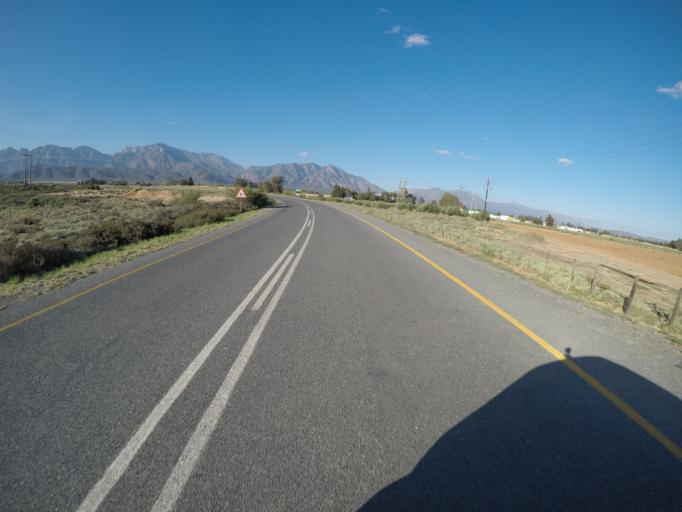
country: ZA
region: Western Cape
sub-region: Cape Winelands District Municipality
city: Worcester
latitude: -33.6717
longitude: 19.5410
